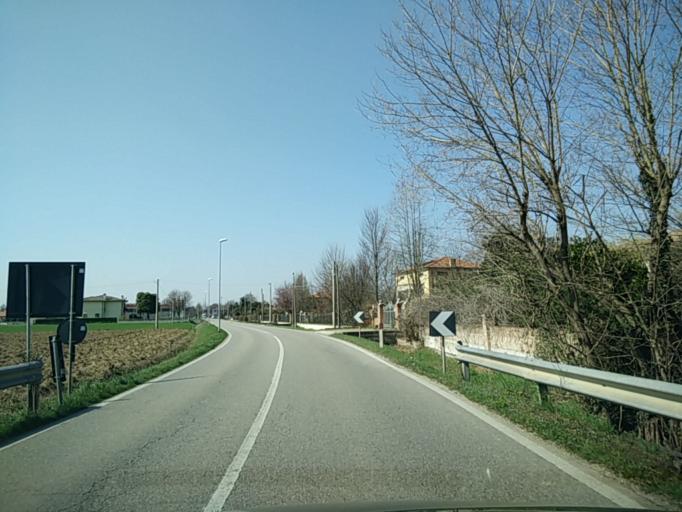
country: IT
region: Veneto
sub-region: Provincia di Treviso
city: Castello di Godego
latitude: 45.6980
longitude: 11.8930
